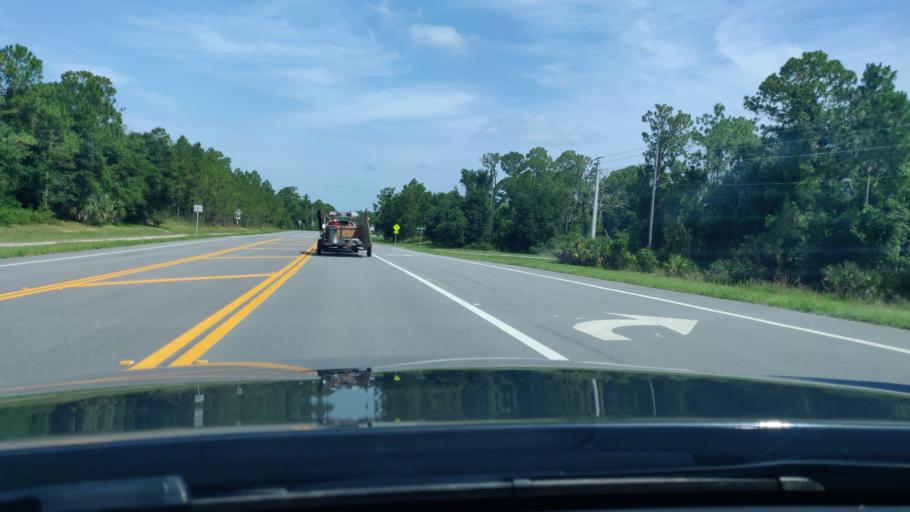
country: US
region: Florida
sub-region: Flagler County
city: Flagler Beach
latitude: 29.5187
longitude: -81.1663
